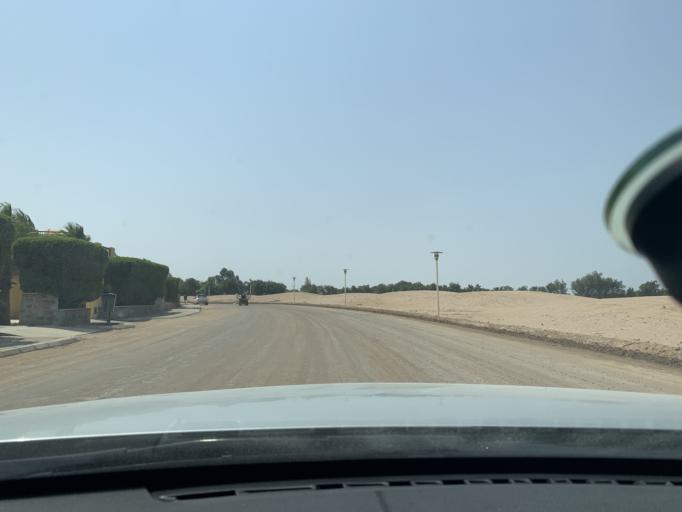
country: EG
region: Red Sea
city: El Gouna
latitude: 27.3888
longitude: 33.6684
